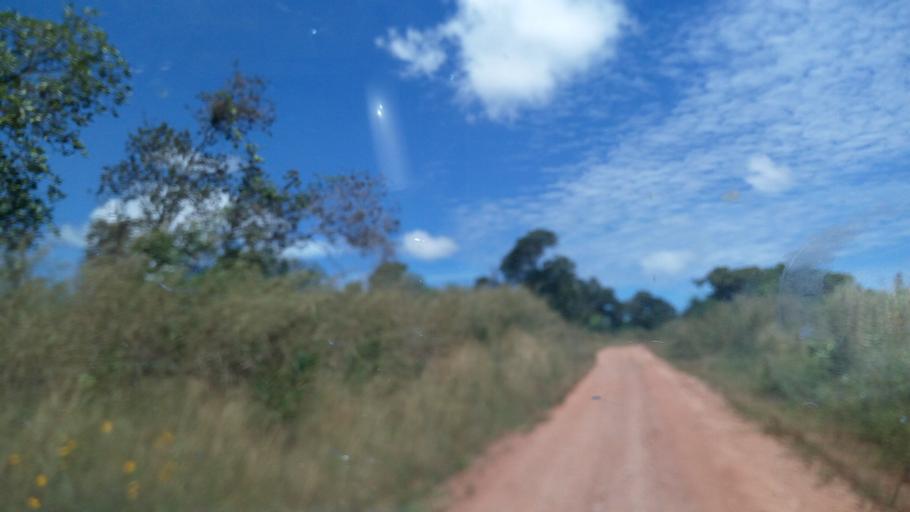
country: CD
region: Katanga
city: Kalemie
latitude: -5.6034
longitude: 29.0358
